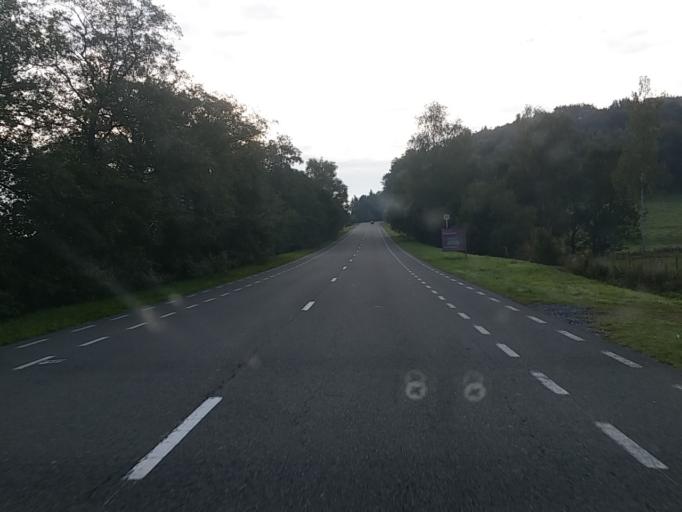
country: BE
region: Wallonia
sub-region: Province du Luxembourg
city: Florenville
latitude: 49.7140
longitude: 5.2541
